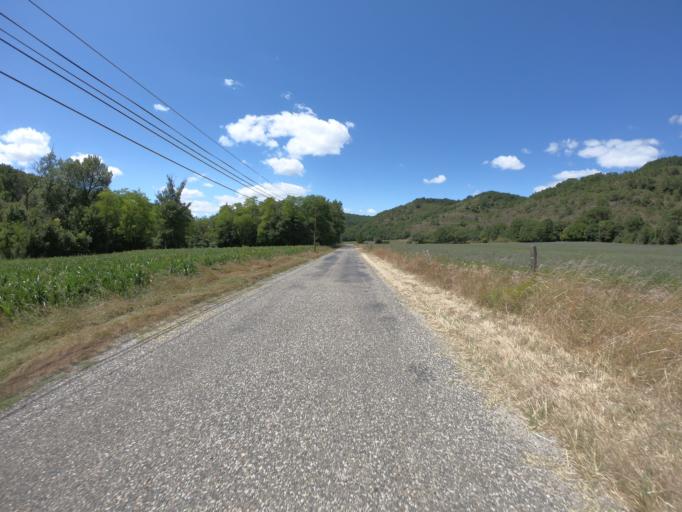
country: FR
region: Midi-Pyrenees
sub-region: Departement de l'Ariege
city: Mirepoix
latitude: 43.0519
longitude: 1.8102
